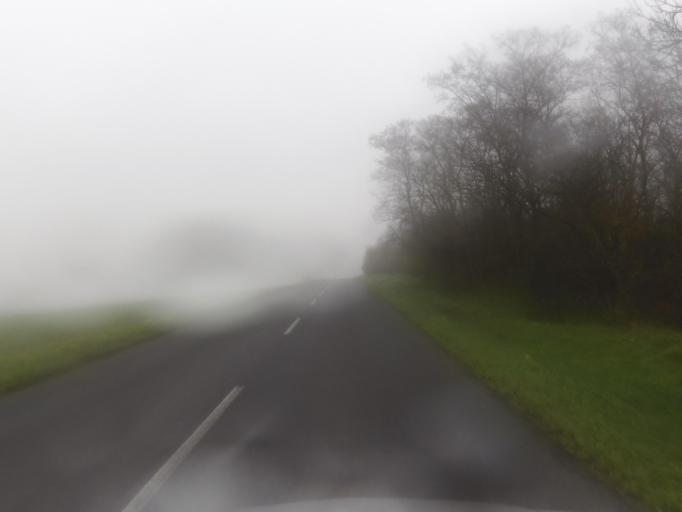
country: CZ
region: Ustecky
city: Postoloprty
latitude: 50.3231
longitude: 13.7294
